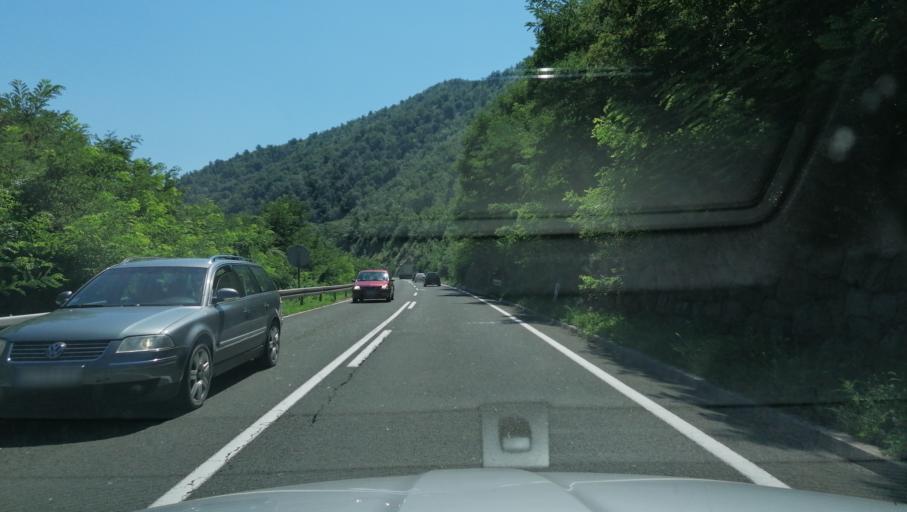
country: RS
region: Central Serbia
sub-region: Raski Okrug
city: Kraljevo
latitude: 43.5931
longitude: 20.5708
